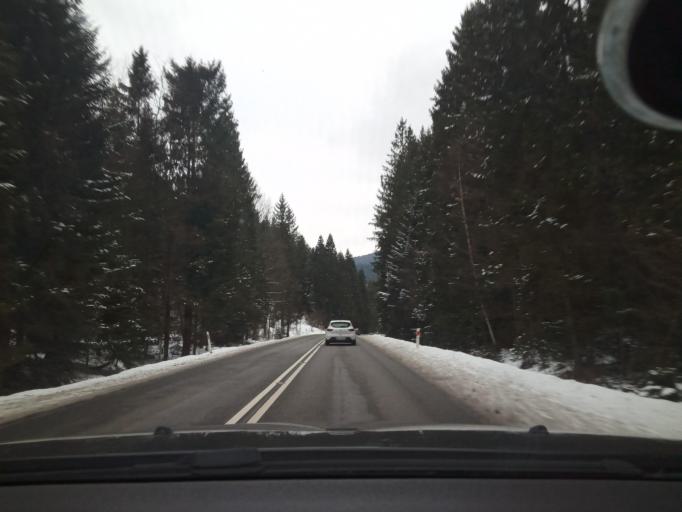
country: PL
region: Lesser Poland Voivodeship
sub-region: Powiat limanowski
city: Lubomierz
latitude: 49.6263
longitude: 20.2595
